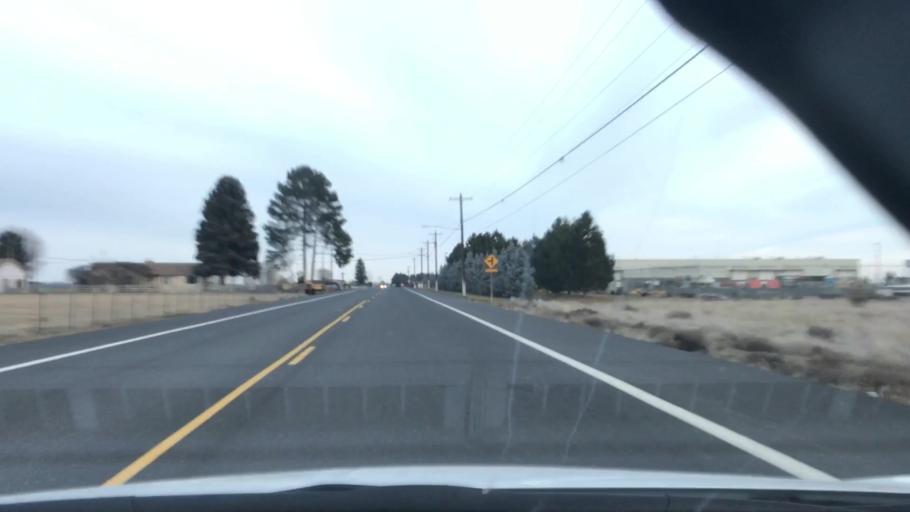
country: US
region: Washington
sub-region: Grant County
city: Moses Lake
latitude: 47.1464
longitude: -119.2449
